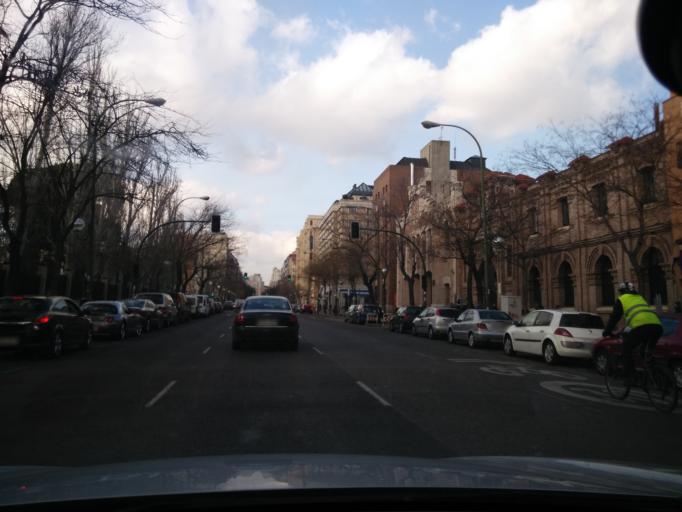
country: ES
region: Madrid
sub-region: Provincia de Madrid
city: Chamberi
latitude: 40.4397
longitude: -3.7008
